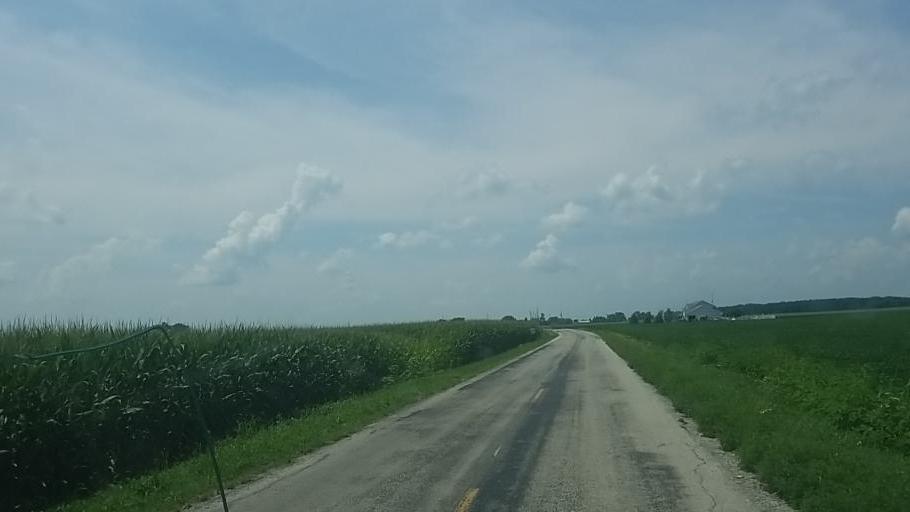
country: US
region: Ohio
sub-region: Marion County
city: Marion
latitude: 40.6737
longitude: -83.2056
